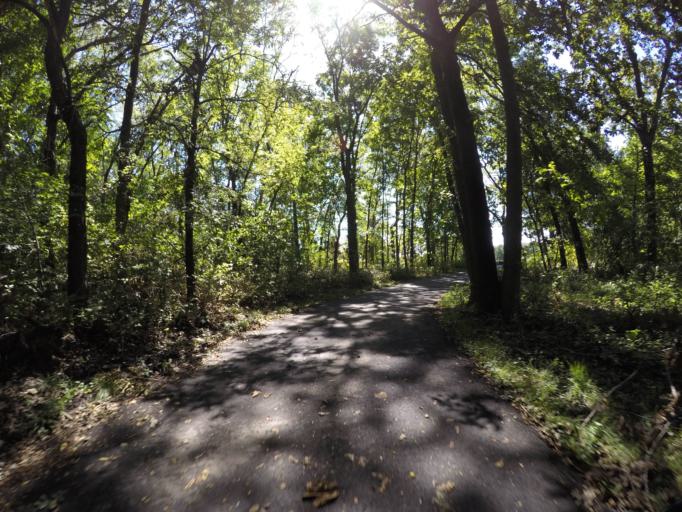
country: US
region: Kansas
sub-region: Johnson County
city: Lenexa
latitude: 38.9205
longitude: -94.6997
